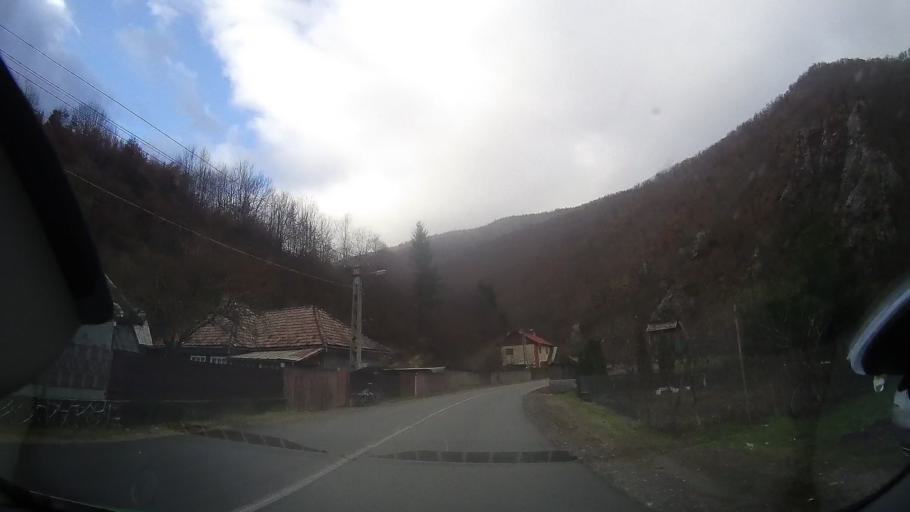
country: RO
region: Cluj
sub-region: Comuna Valea Ierii
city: Valea Ierii
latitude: 46.6852
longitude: 23.2788
